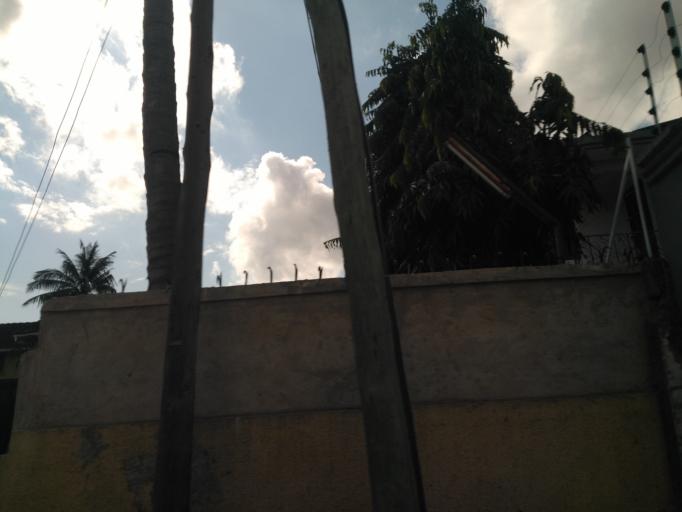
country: TZ
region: Dar es Salaam
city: Magomeni
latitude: -6.7653
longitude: 39.2477
